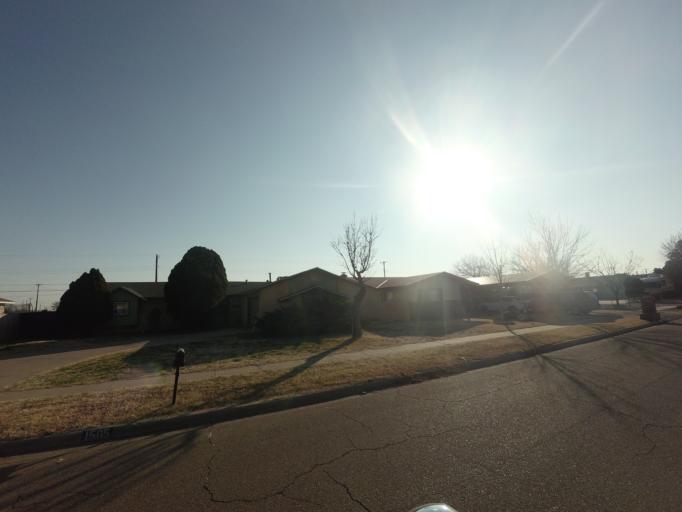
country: US
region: New Mexico
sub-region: Curry County
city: Clovis
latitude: 34.4143
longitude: -103.2125
